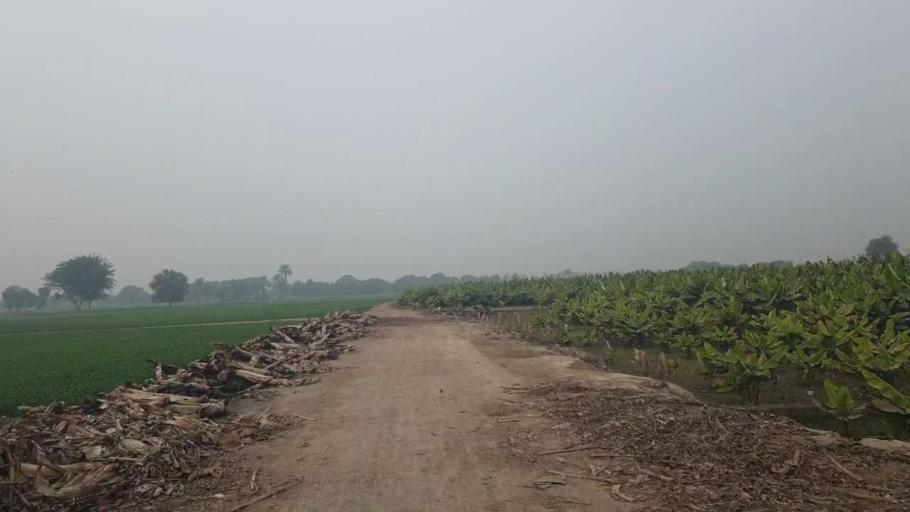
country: PK
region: Sindh
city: Tando Adam
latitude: 25.7215
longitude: 68.6289
